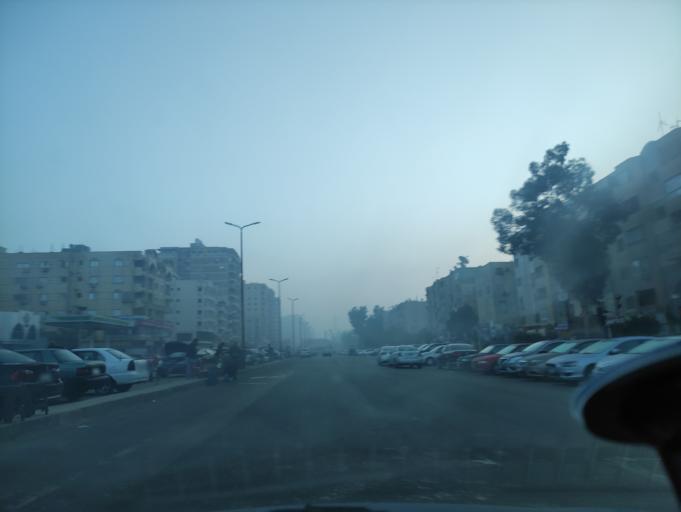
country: EG
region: Muhafazat al Qahirah
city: Cairo
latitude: 30.0469
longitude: 31.3597
